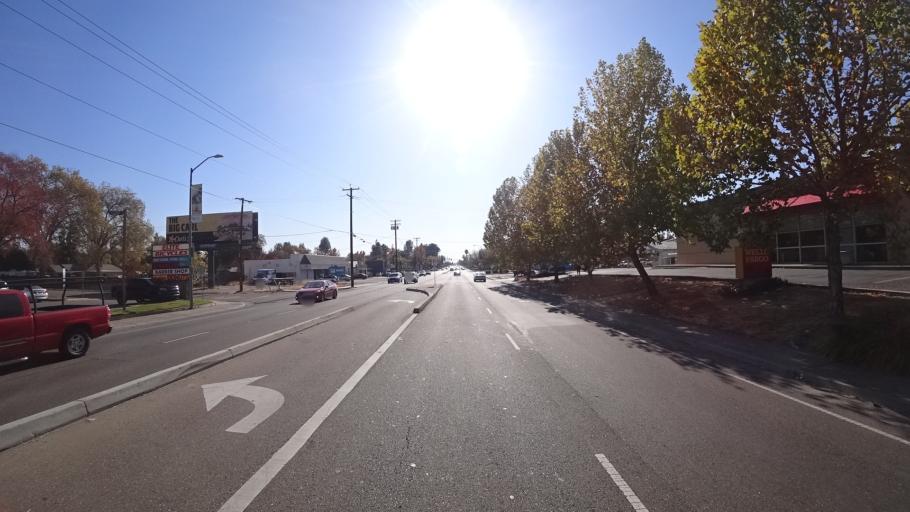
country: US
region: California
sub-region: Sacramento County
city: Citrus Heights
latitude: 38.7206
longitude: -121.2905
